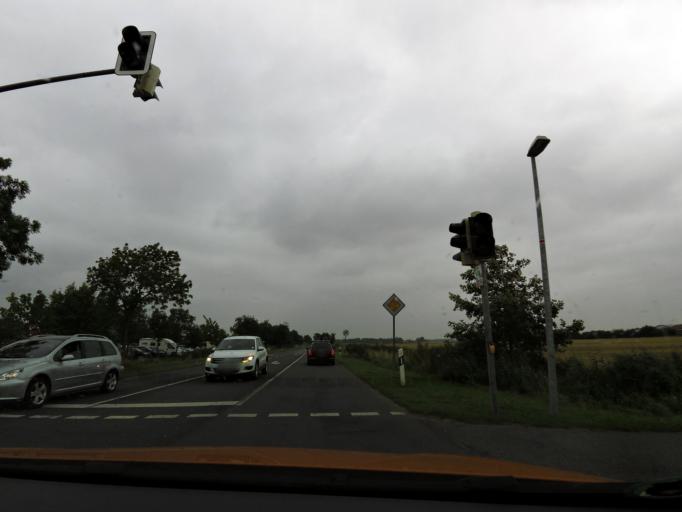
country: DE
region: Lower Saxony
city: Wirdum
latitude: 53.4969
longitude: 7.1028
